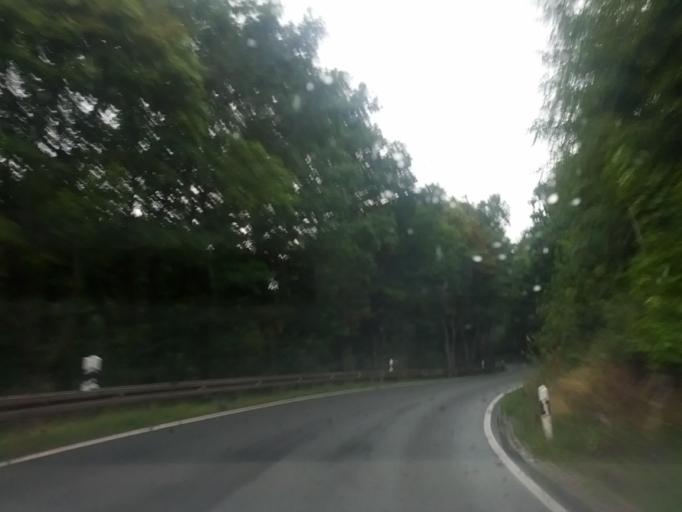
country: DE
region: Thuringia
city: Tabarz
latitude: 50.8896
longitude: 10.4962
